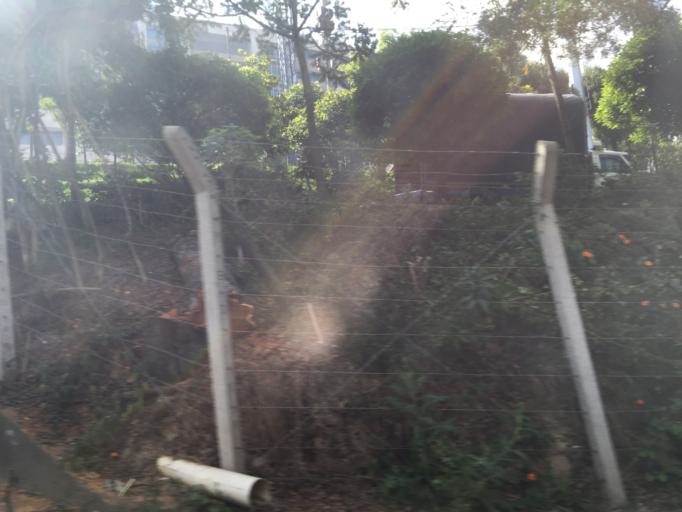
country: CO
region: Bogota D.C.
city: Bogota
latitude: 4.5980
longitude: -74.0673
